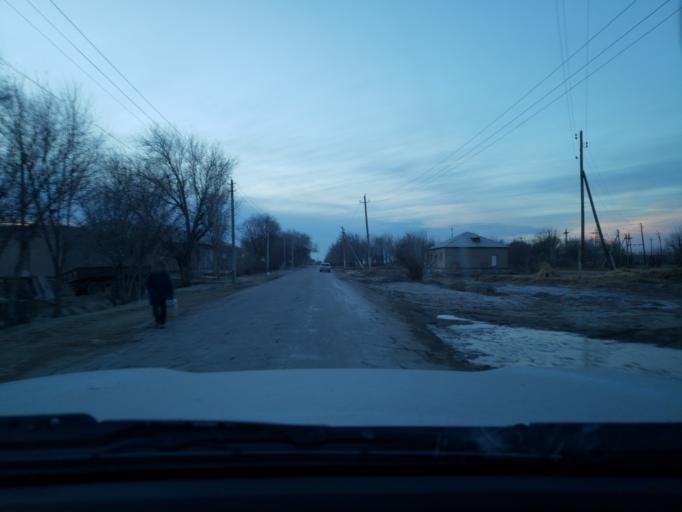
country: TM
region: Dasoguz
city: Tagta
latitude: 41.5847
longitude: 60.0592
